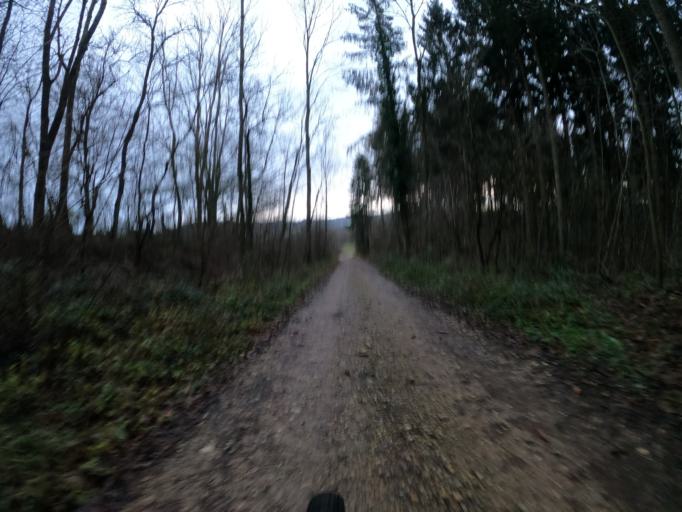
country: DE
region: Baden-Wuerttemberg
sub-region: Regierungsbezirk Stuttgart
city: Sussen
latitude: 48.7022
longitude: 9.7776
